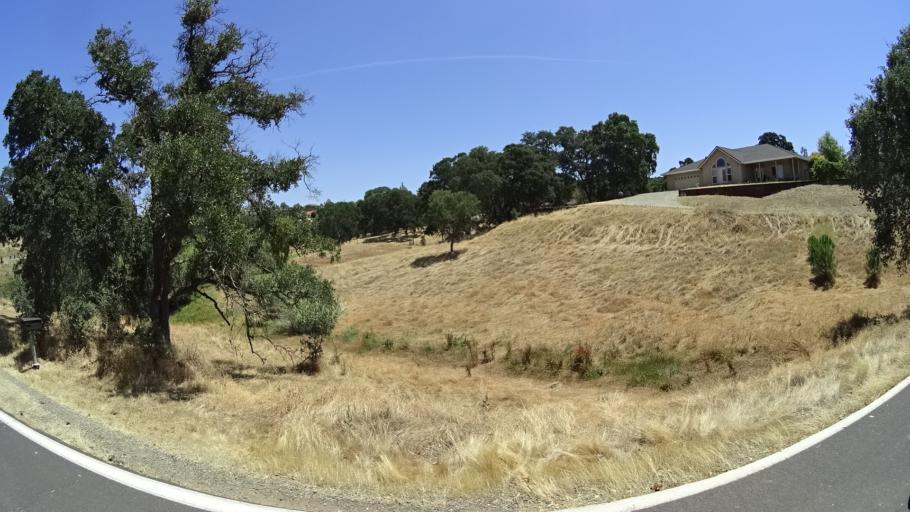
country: US
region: California
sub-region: Calaveras County
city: Rancho Calaveras
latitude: 38.1288
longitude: -120.8661
